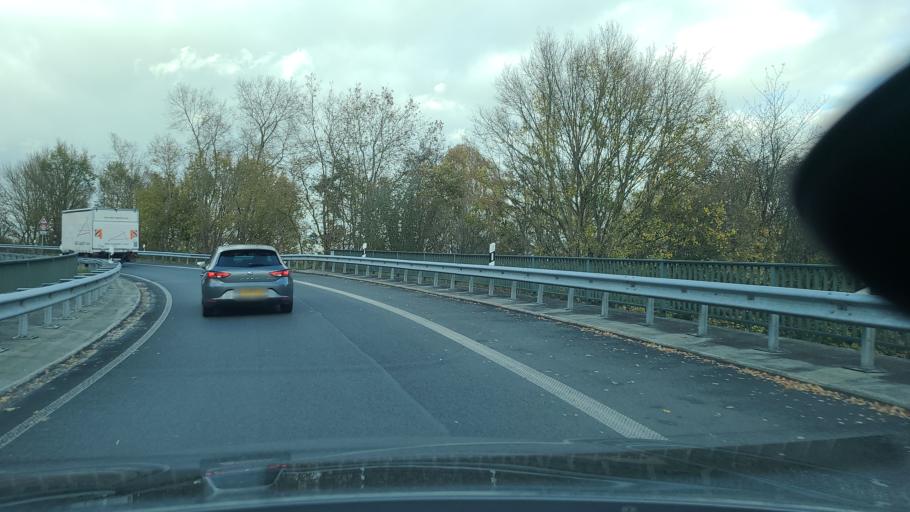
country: DE
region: North Rhine-Westphalia
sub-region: Regierungsbezirk Dusseldorf
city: Kranenburg
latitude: 51.8004
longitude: 6.0250
